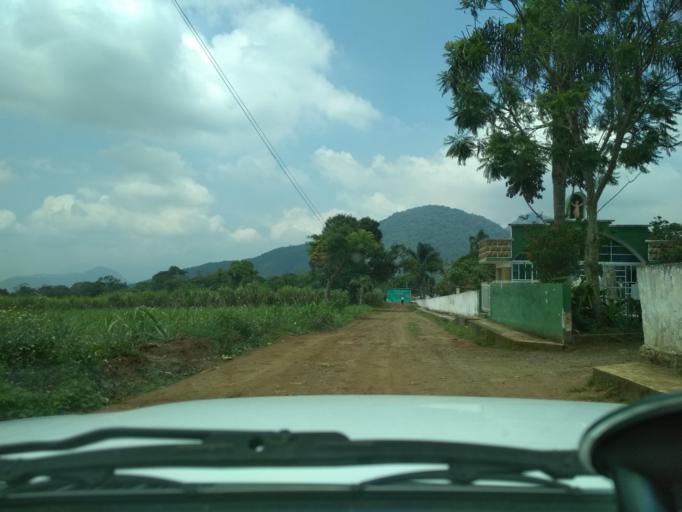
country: MX
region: Veracruz
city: Monte Blanco
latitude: 18.9594
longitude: -97.0225
